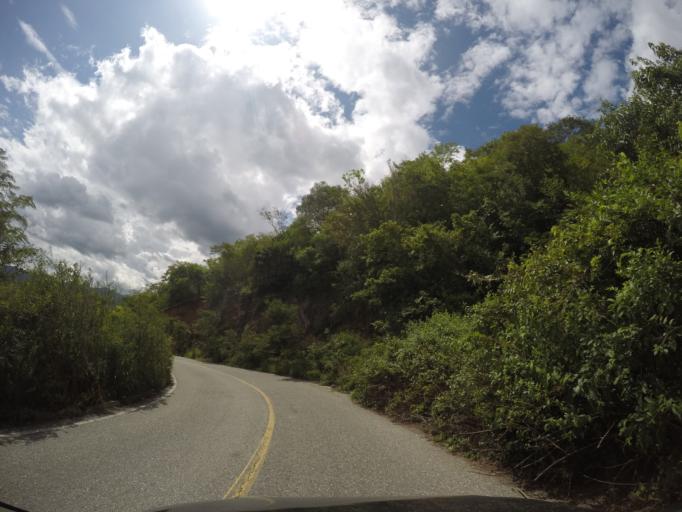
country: MX
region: Oaxaca
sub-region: San Jeronimo Coatlan
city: San Cristobal Honduras
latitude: 16.4325
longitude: -97.0467
